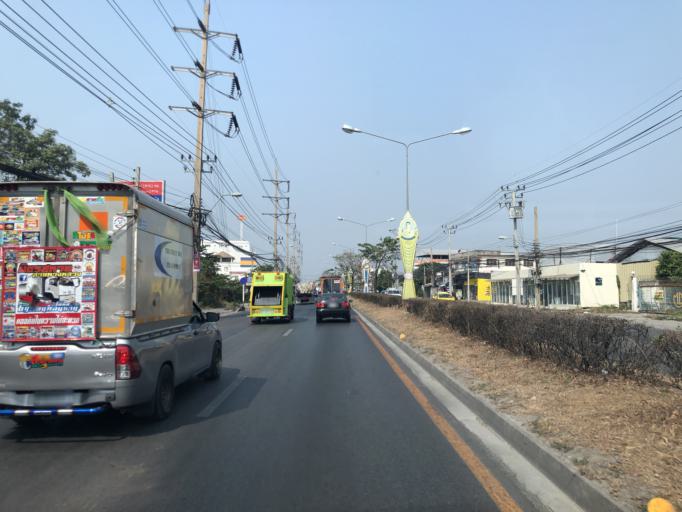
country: TH
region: Samut Prakan
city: Bang Bo District
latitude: 13.5956
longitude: 100.7526
